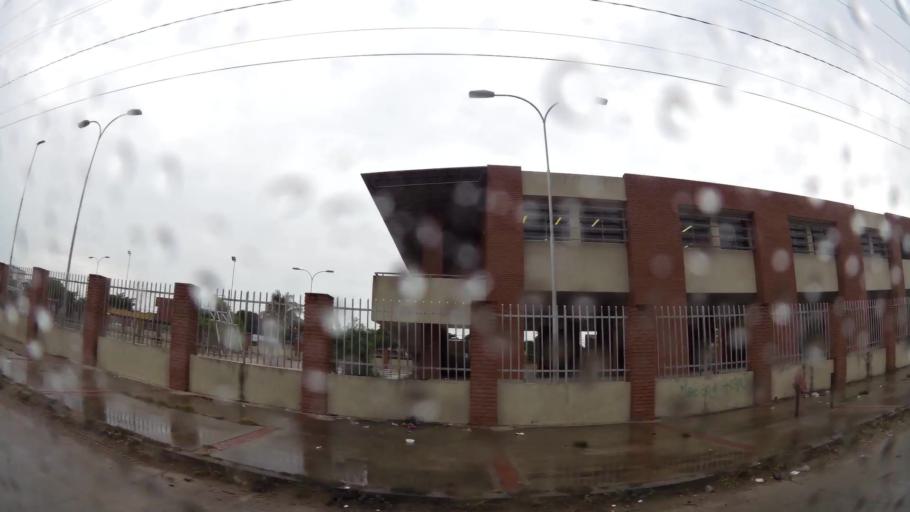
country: BO
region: Santa Cruz
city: Santa Cruz de la Sierra
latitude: -17.8020
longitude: -63.1305
